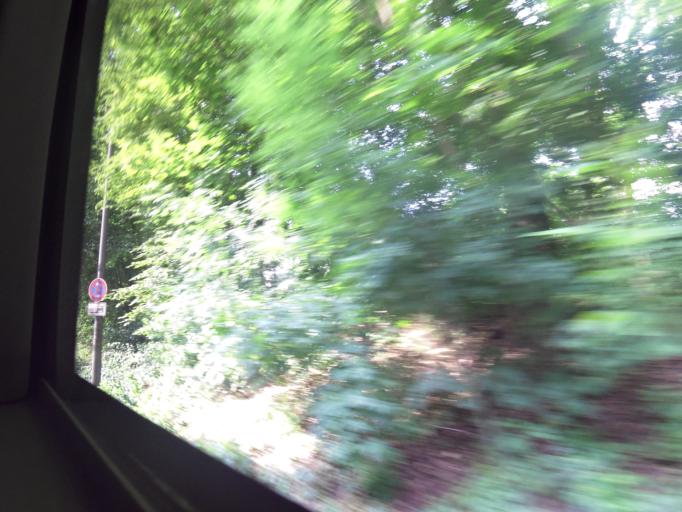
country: DE
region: Bavaria
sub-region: Regierungsbezirk Mittelfranken
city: Nuernberg
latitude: 49.4337
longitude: 11.1024
